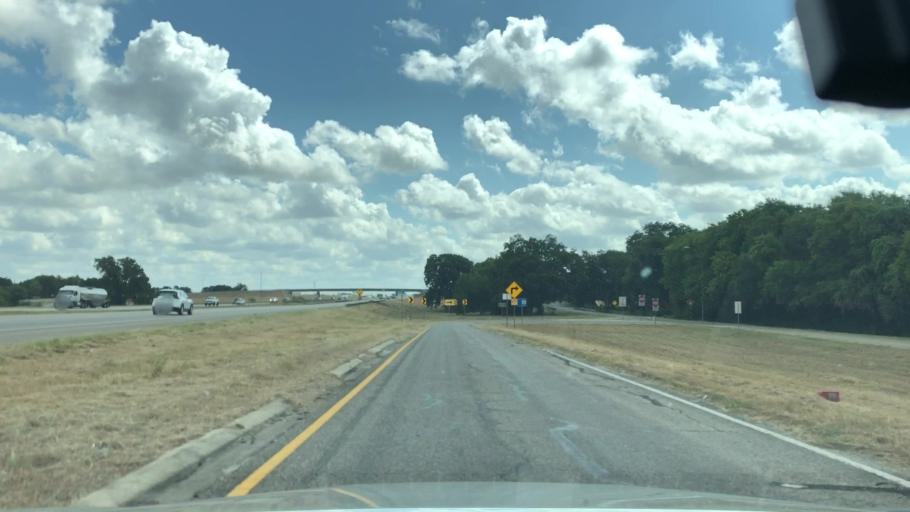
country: US
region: Texas
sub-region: Guadalupe County
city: McQueeney
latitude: 29.5686
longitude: -98.0200
